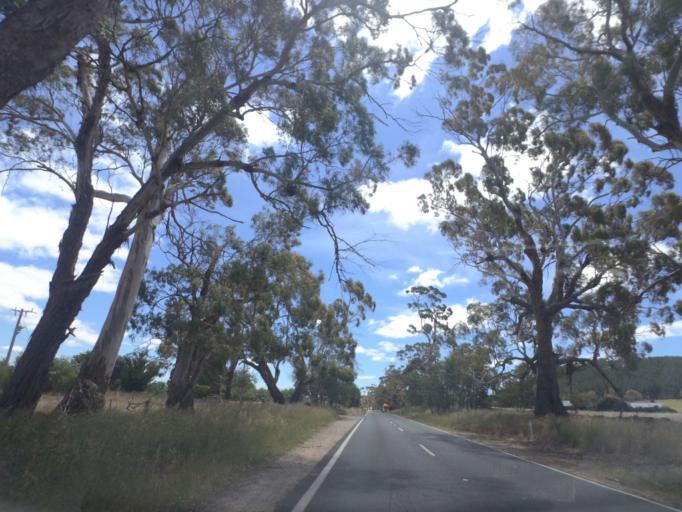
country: AU
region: Victoria
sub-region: Mount Alexander
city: Castlemaine
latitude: -37.2754
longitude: 144.1478
